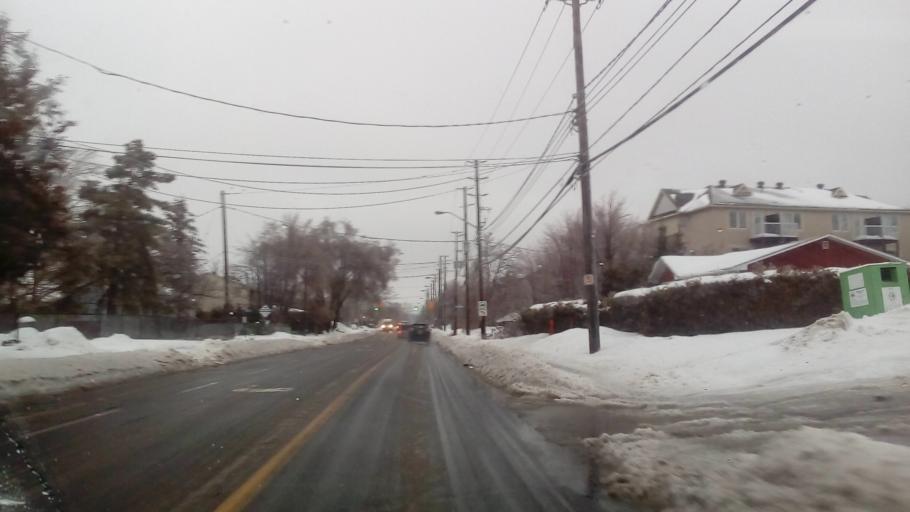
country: CA
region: Ontario
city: Ottawa
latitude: 45.4267
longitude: -75.6319
